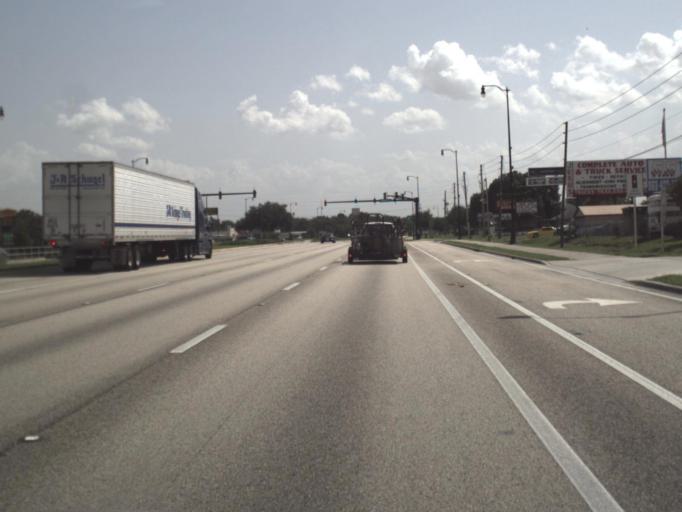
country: US
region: Florida
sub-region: Polk County
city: Haines City
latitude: 28.1191
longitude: -81.6398
